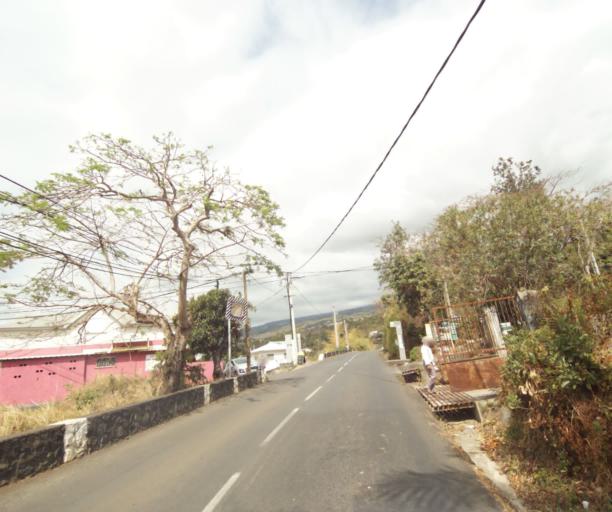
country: RE
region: Reunion
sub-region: Reunion
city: Saint-Paul
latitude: -21.0218
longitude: 55.2903
